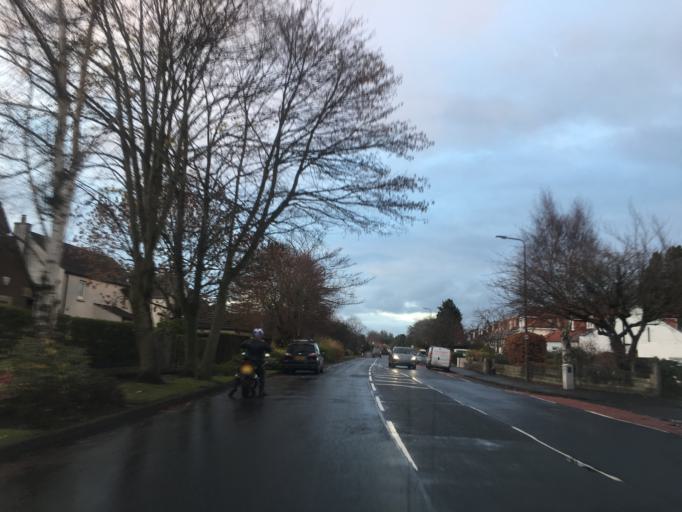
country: GB
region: Scotland
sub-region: Edinburgh
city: Colinton
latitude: 55.9569
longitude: -3.2667
